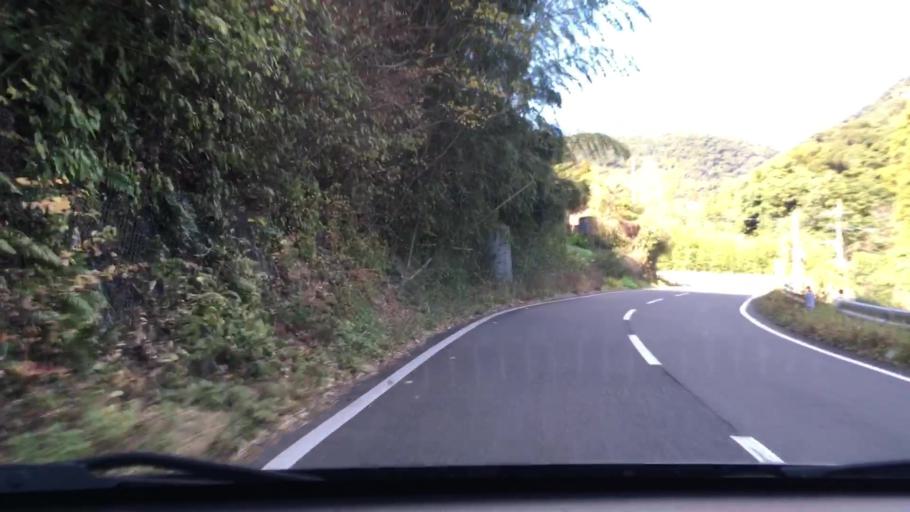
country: JP
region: Kagoshima
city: Ijuin
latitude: 31.7152
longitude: 130.4339
